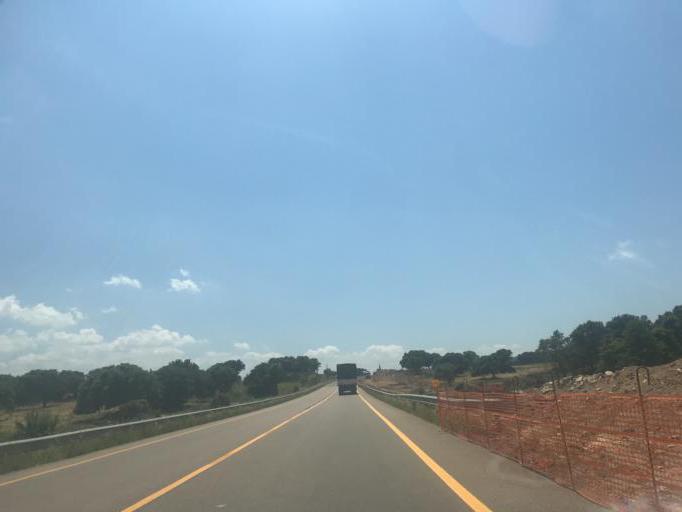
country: IT
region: Sardinia
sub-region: Provincia di Olbia-Tempio
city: Monti
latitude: 40.7830
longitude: 9.2492
